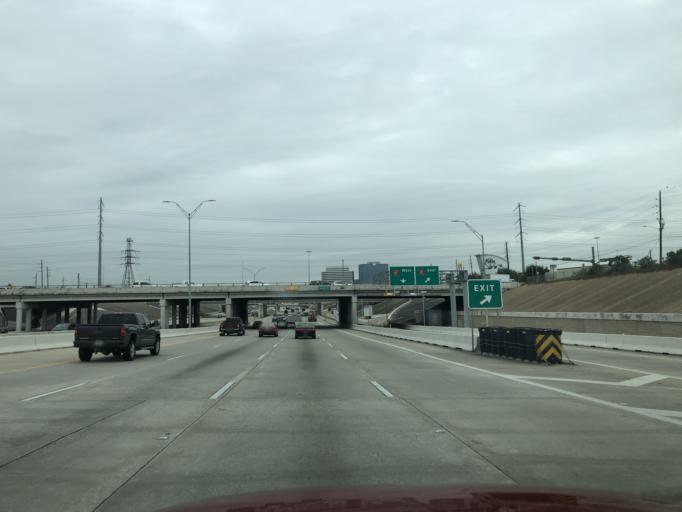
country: US
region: Texas
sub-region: Harris County
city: Bunker Hill Village
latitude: 29.7154
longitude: -95.5572
